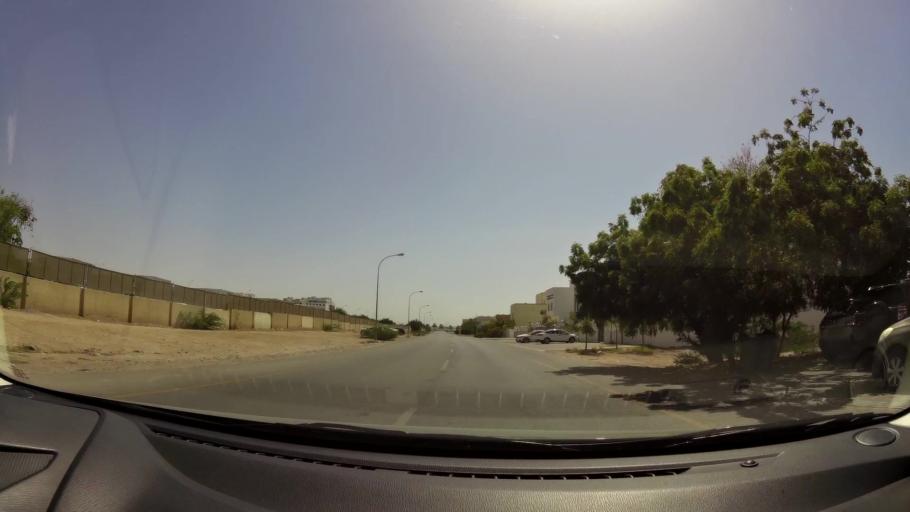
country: OM
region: Muhafazat Masqat
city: Bawshar
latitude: 23.5970
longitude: 58.3540
